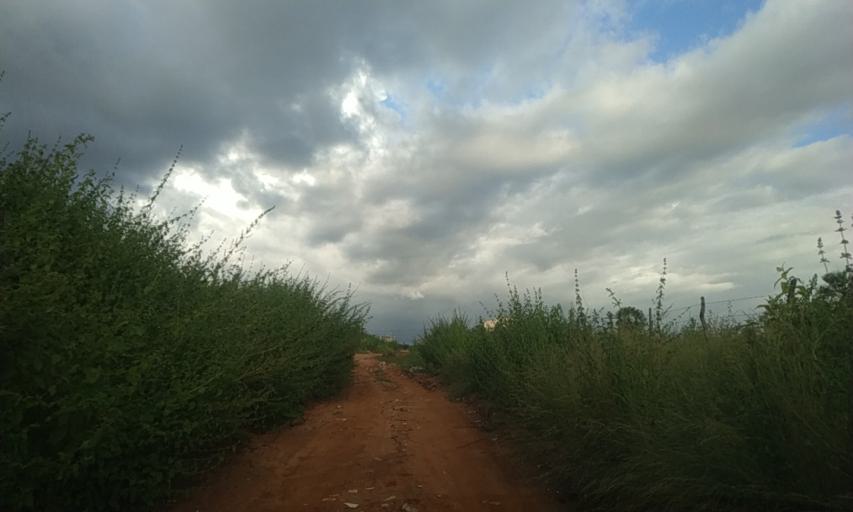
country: BR
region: Rio Grande do Norte
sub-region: Mossoro
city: Mossoro
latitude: -5.2206
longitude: -37.3441
